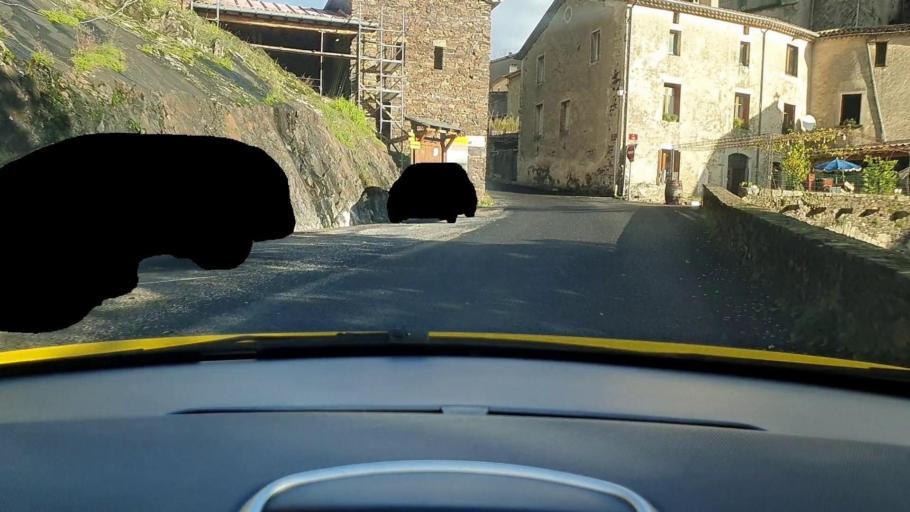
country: FR
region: Languedoc-Roussillon
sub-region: Departement du Gard
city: Sumene
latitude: 44.0337
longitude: 3.7352
